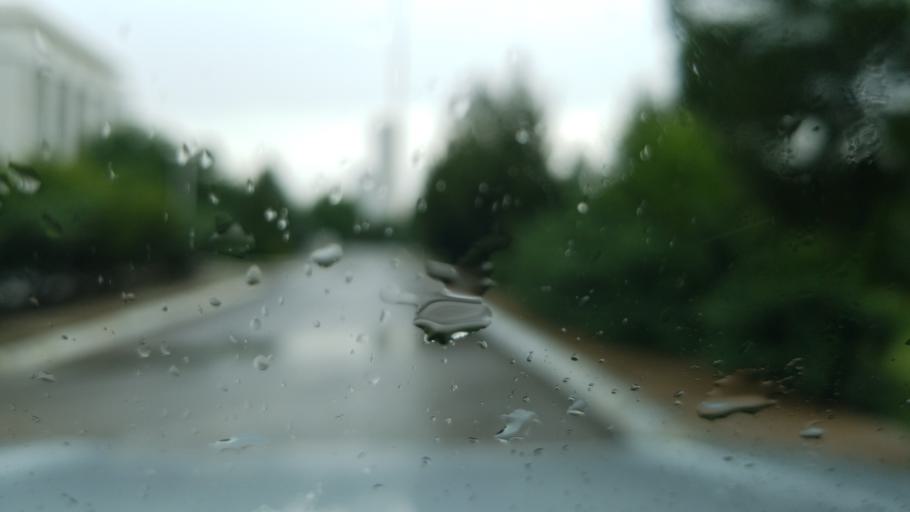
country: TM
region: Ahal
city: Ashgabat
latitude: 37.8853
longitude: 58.3536
